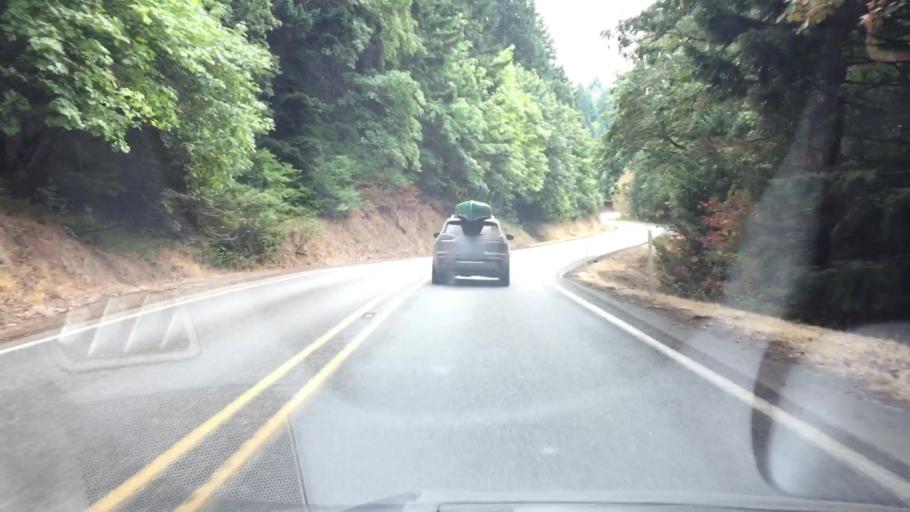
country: US
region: Washington
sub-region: Klickitat County
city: White Salmon
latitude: 45.7502
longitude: -121.5179
